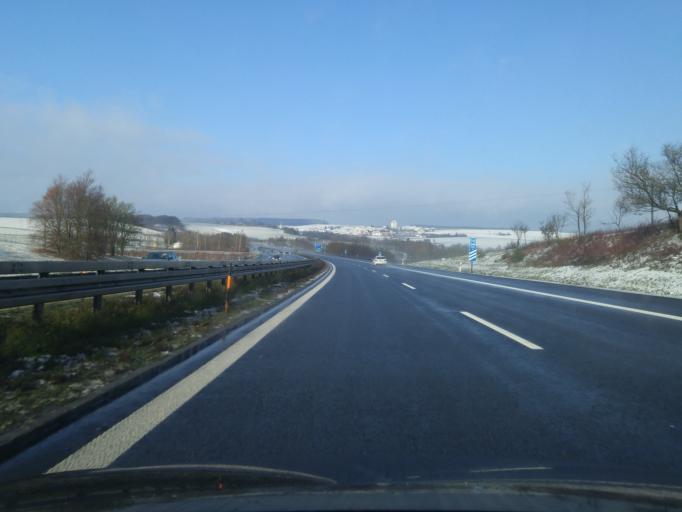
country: DE
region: Bavaria
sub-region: Regierungsbezirk Unterfranken
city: Wasserlosen
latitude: 50.0609
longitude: 10.0502
